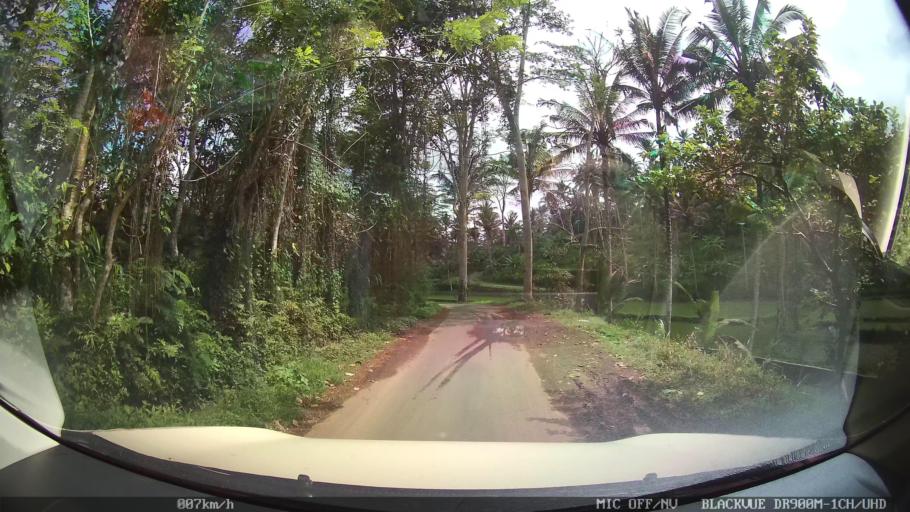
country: ID
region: Bali
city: Banjar Petak
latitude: -8.4485
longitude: 115.3268
